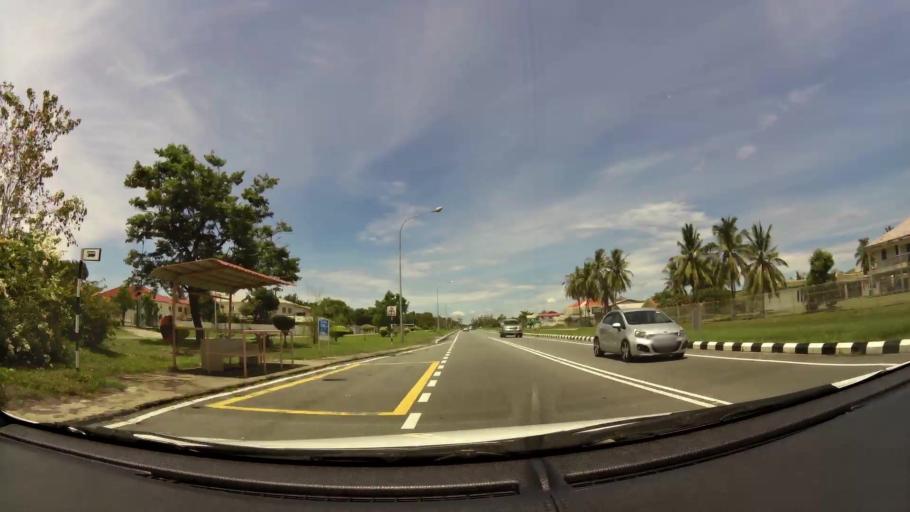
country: BN
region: Belait
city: Kuala Belait
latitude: 4.5930
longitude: 114.2313
